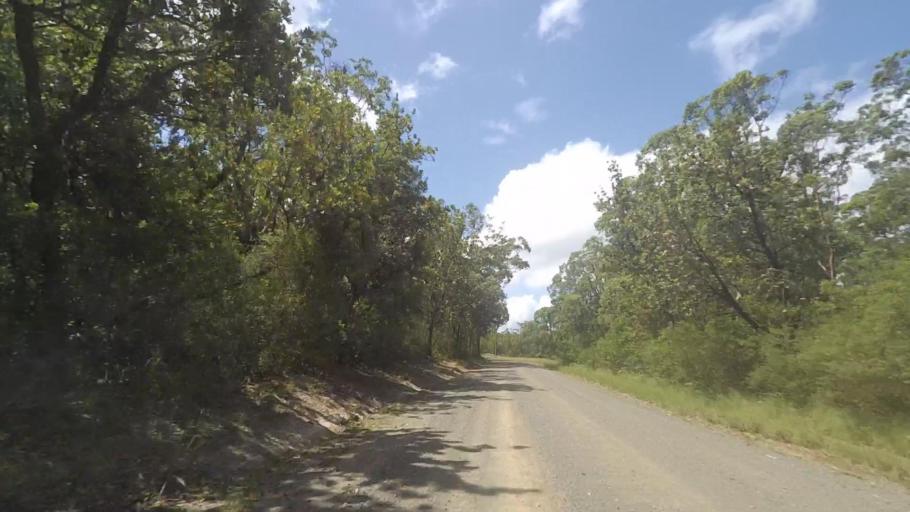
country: AU
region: New South Wales
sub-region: Great Lakes
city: Bulahdelah
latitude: -32.5084
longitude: 152.2924
